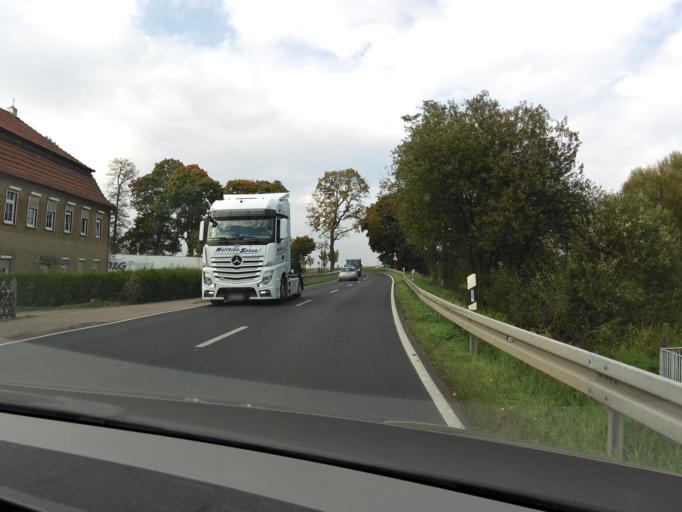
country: DE
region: Thuringia
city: Breitungen
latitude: 50.7740
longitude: 10.3154
